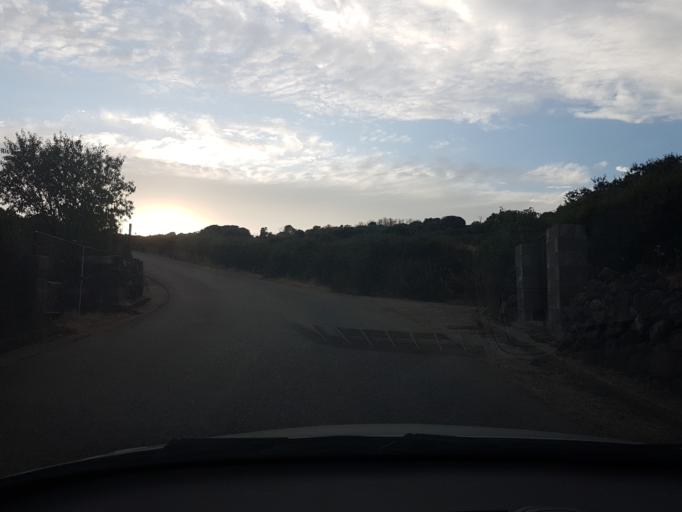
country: IT
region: Sardinia
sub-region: Provincia di Oristano
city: Seneghe
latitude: 40.0983
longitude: 8.6257
